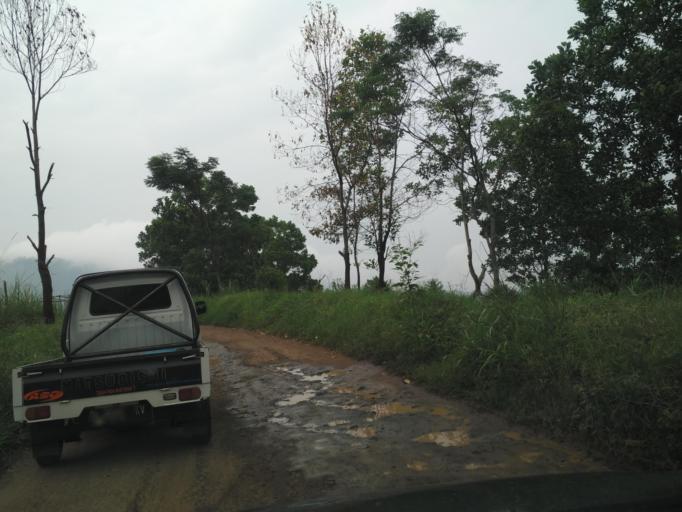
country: ID
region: West Java
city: Caringin
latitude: -6.6744
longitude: 107.0201
